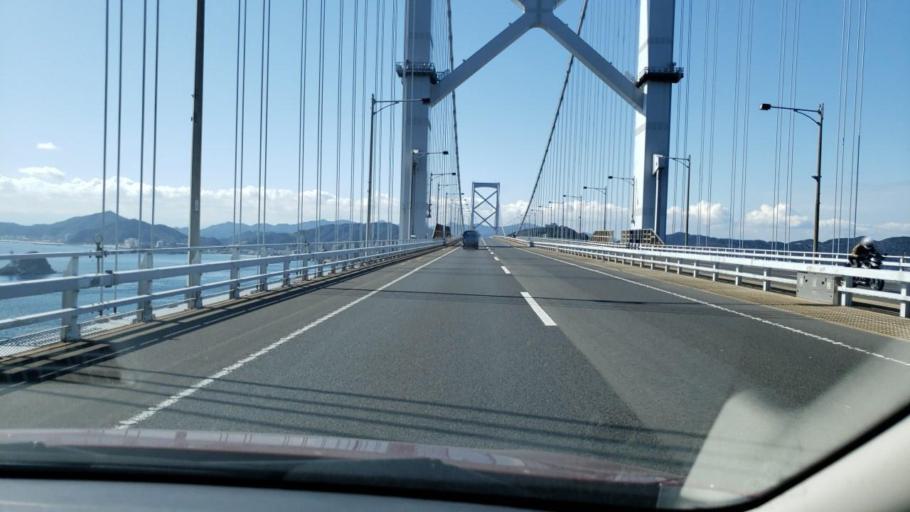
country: JP
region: Tokushima
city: Narutocho-mitsuishi
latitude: 34.2373
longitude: 134.6496
